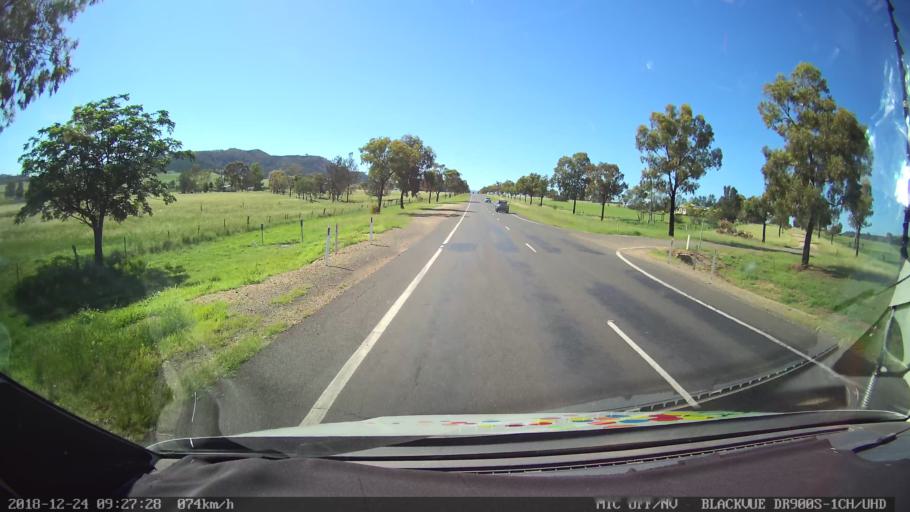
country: AU
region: New South Wales
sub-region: Liverpool Plains
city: Quirindi
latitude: -31.5283
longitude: 150.6813
